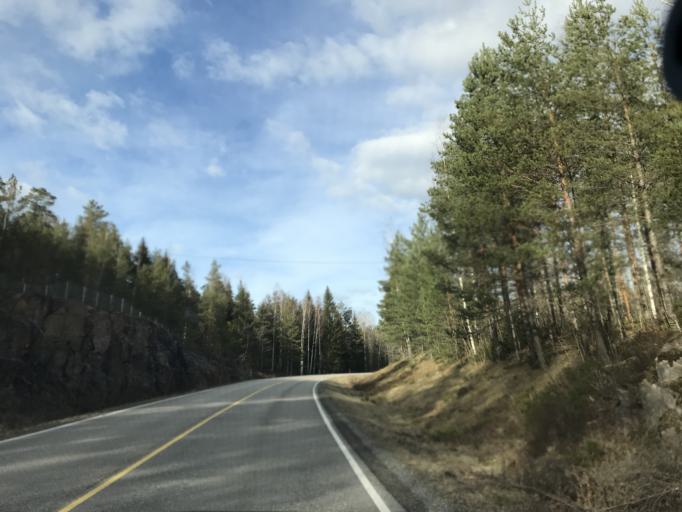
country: FI
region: Uusimaa
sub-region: Raaseporin
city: Ekenaes
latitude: 60.0786
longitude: 23.3523
